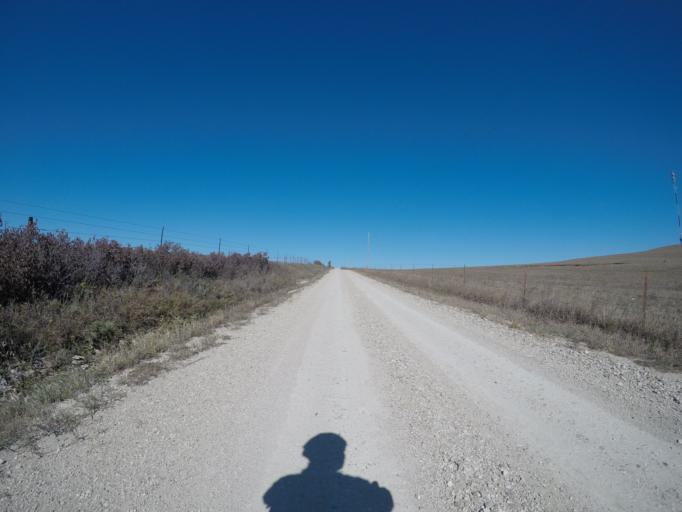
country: US
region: Kansas
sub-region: Wabaunsee County
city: Alma
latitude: 39.0248
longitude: -96.3722
